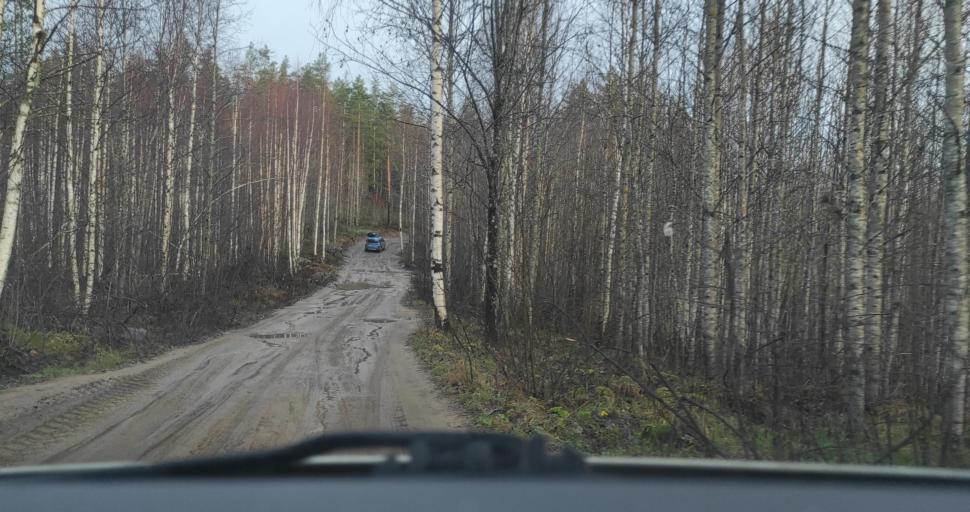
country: RU
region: Republic of Karelia
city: Pitkyaranta
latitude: 61.7413
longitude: 31.3918
